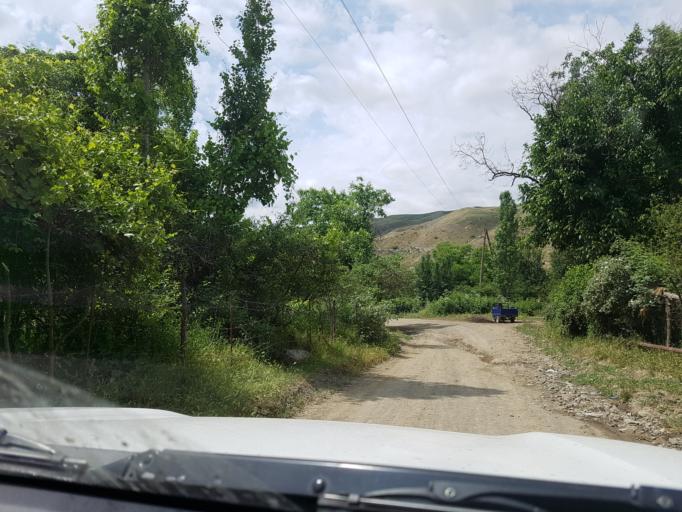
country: TM
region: Ahal
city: Baharly
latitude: 38.1984
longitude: 57.0041
